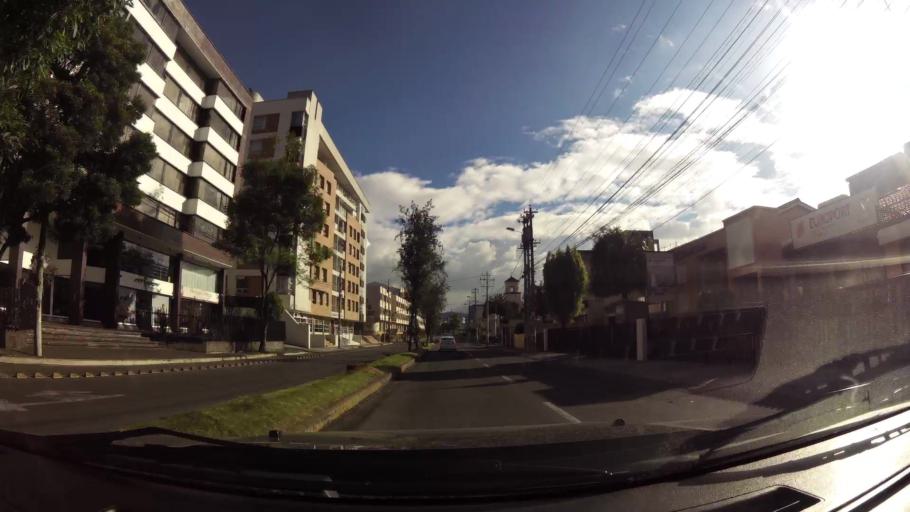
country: EC
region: Pichincha
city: Quito
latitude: -0.2069
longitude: -78.4864
